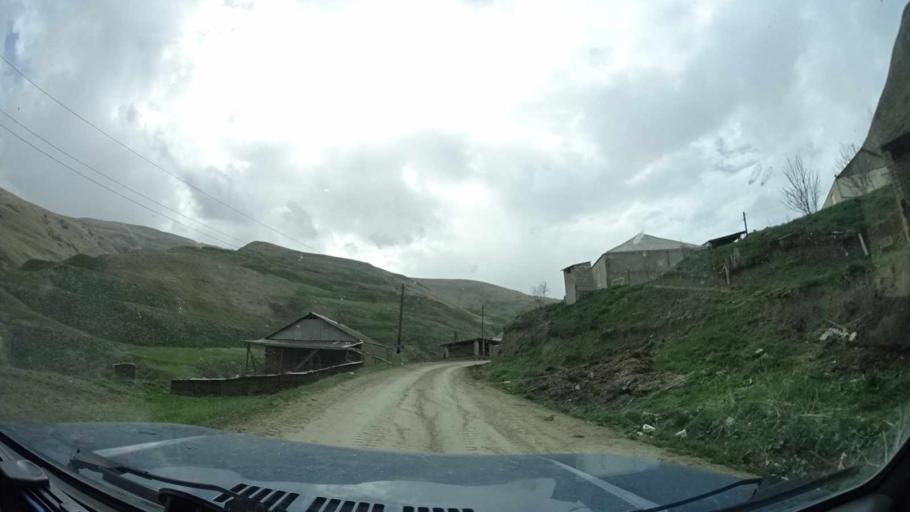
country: RU
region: Dagestan
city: Usisha
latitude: 42.1331
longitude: 47.3663
